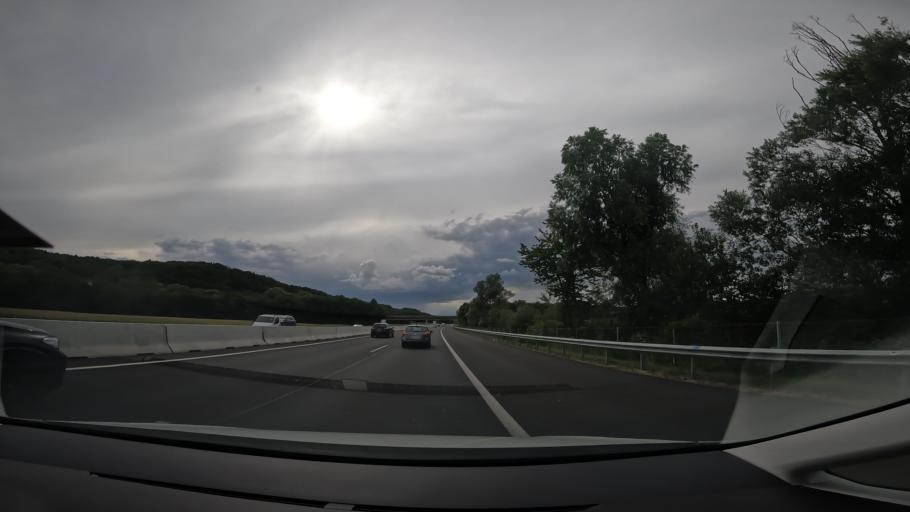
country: AT
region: Styria
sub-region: Politischer Bezirk Hartberg-Fuerstenfeld
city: Ilz
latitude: 47.0769
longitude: 15.9478
